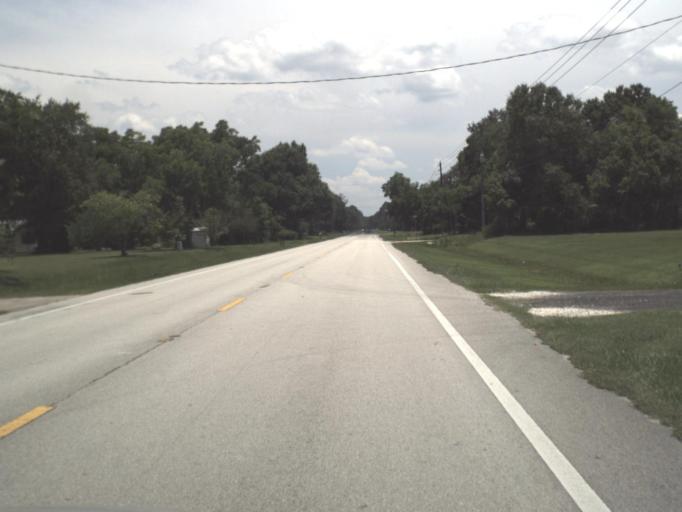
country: US
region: Florida
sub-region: Bradford County
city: Starke
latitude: 30.0111
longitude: -82.1427
